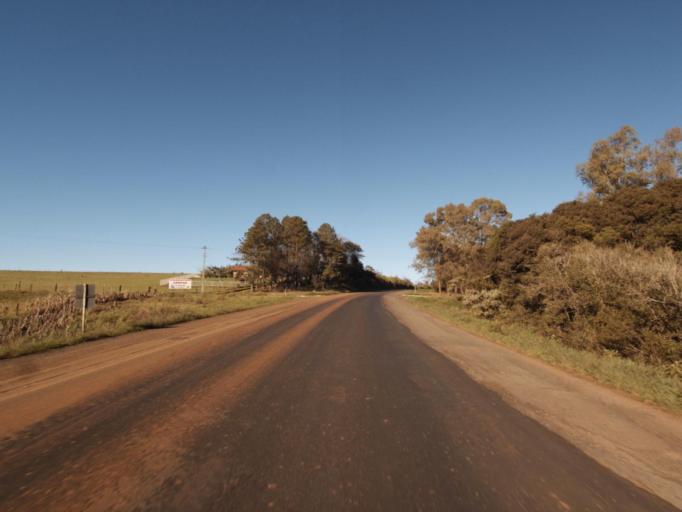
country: BR
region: Rio Grande do Sul
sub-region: Frederico Westphalen
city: Frederico Westphalen
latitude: -26.9129
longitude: -53.1879
